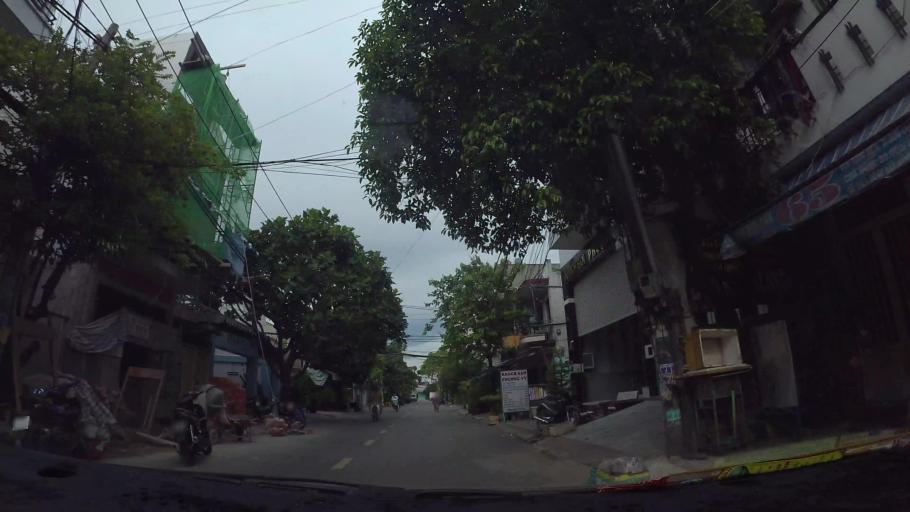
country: VN
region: Ho Chi Minh City
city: Quan Ba
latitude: 10.7696
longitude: 106.6885
